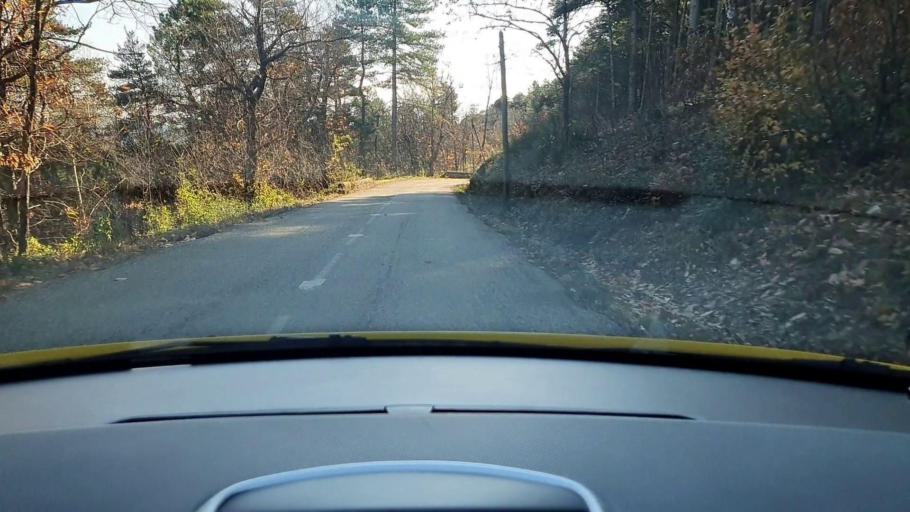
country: FR
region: Languedoc-Roussillon
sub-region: Departement du Gard
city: Branoux-les-Taillades
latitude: 44.2871
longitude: 3.9407
